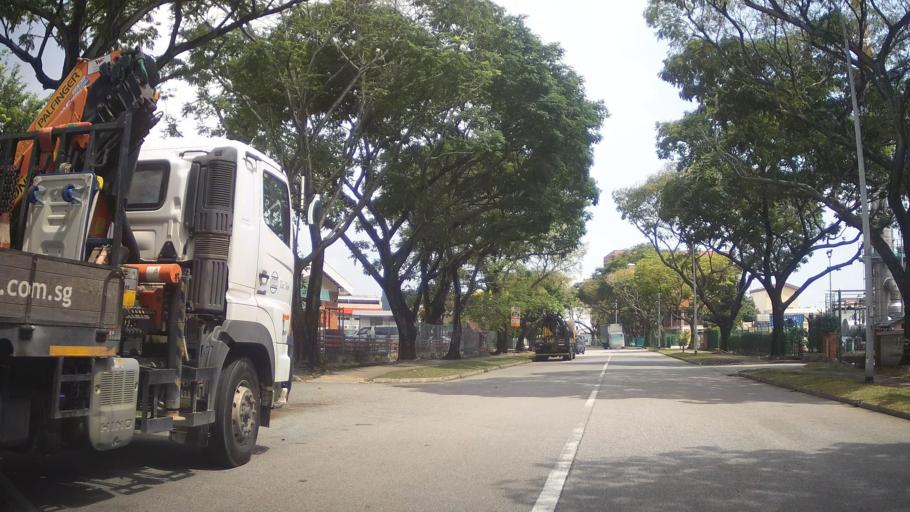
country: MY
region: Johor
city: Johor Bahru
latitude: 1.3106
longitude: 103.6624
